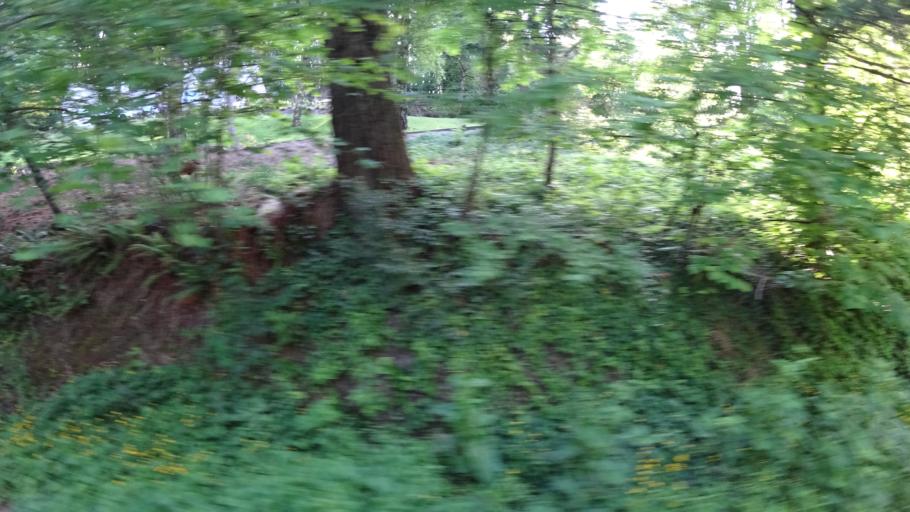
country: US
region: Oregon
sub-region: Washington County
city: West Slope
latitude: 45.5041
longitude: -122.7350
